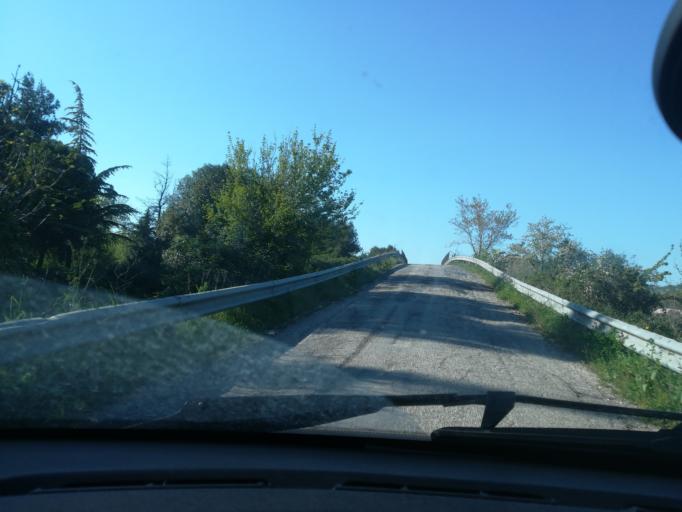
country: IT
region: The Marches
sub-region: Provincia di Macerata
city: Zona Industriale
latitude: 43.2666
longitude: 13.4935
